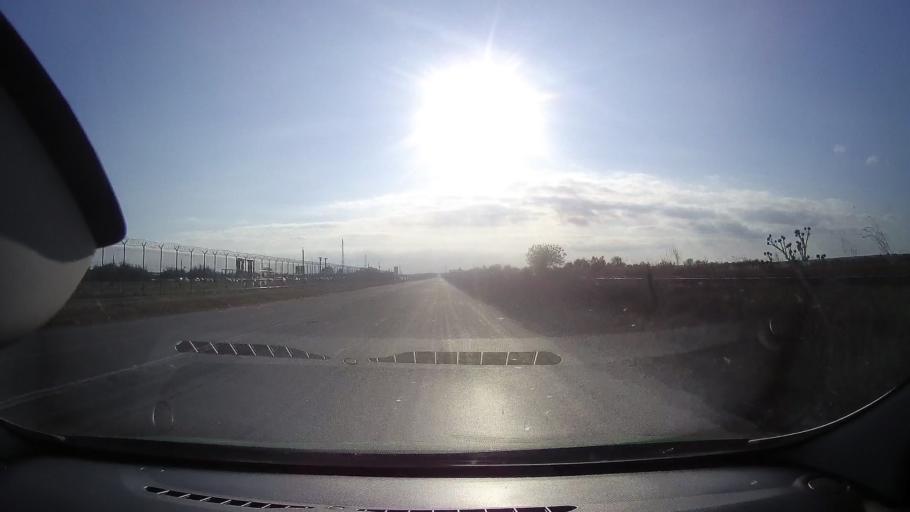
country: RO
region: Constanta
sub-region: Comuna Corbu
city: Corbu
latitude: 44.3403
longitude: 28.6382
